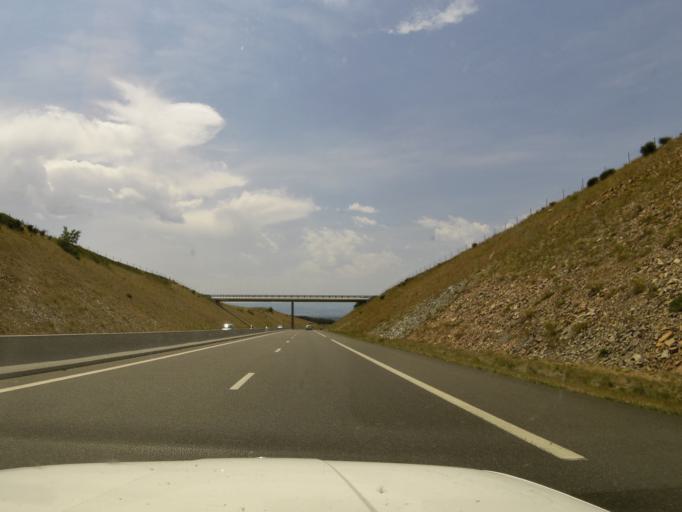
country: FR
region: Rhone-Alpes
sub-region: Departement de la Loire
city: Balbigny
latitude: 45.8443
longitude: 4.2102
